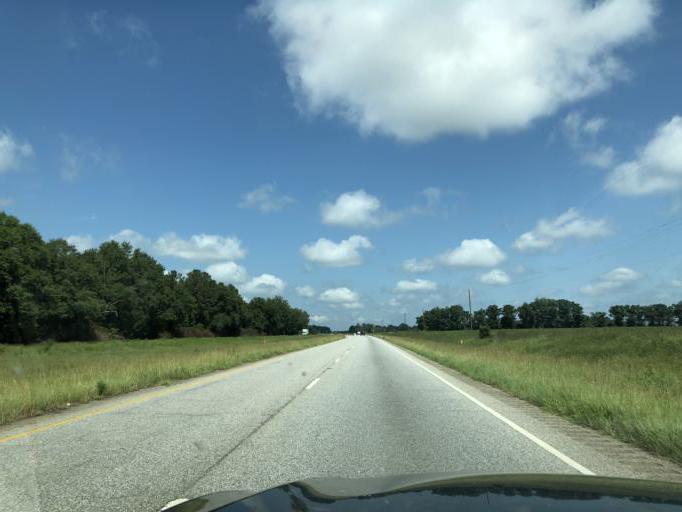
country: US
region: Alabama
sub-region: Henry County
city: Abbeville
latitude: 31.6080
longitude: -85.2770
